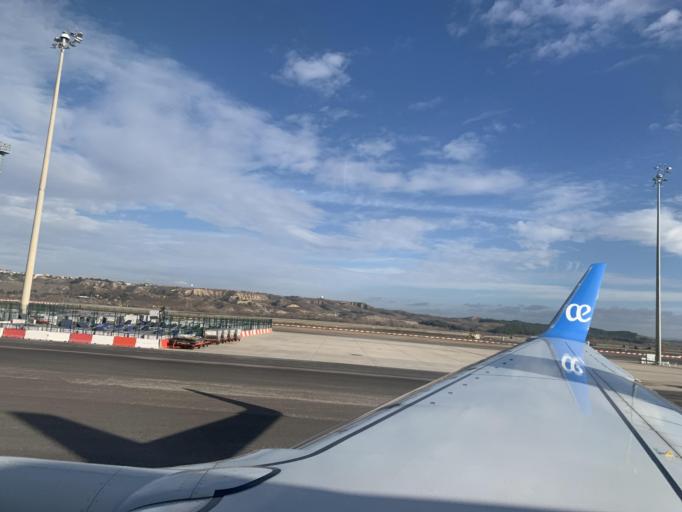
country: ES
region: Madrid
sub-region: Provincia de Madrid
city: Barajas de Madrid
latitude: 40.4905
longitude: -3.5646
